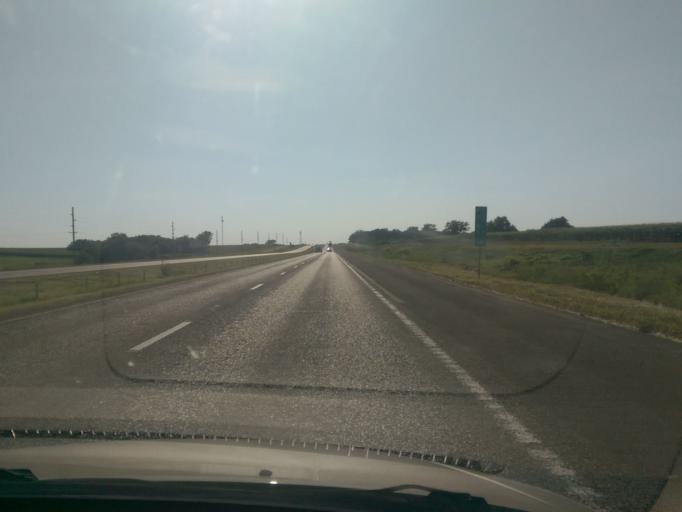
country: US
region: Missouri
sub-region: Lafayette County
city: Concordia
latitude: 38.9920
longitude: -93.6561
